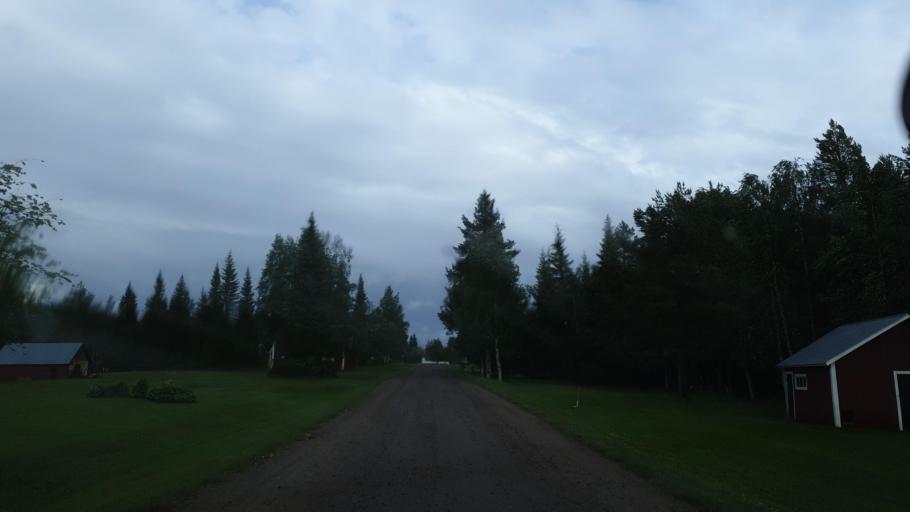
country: SE
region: Norrbotten
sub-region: Arvidsjaurs Kommun
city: Arvidsjaur
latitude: 65.7083
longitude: 18.7069
